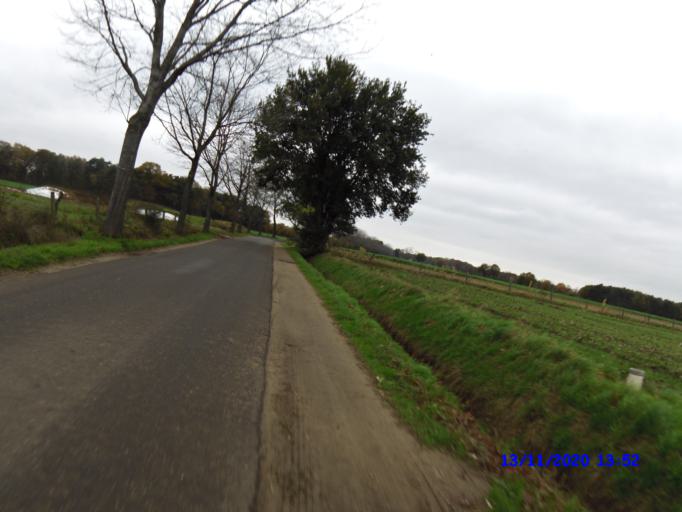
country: BE
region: Flanders
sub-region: Provincie Antwerpen
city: Kasterlee
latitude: 51.2790
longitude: 4.9702
